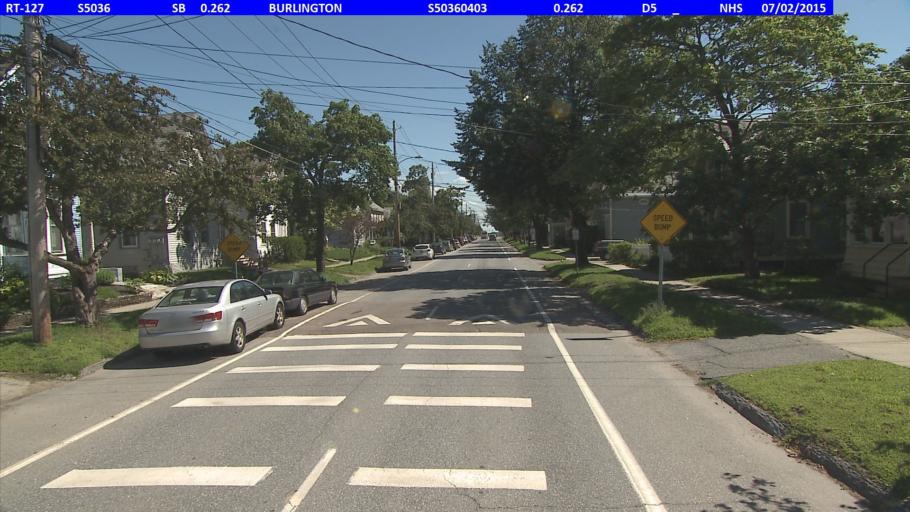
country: US
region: Vermont
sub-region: Chittenden County
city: Burlington
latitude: 44.4842
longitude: -73.2193
